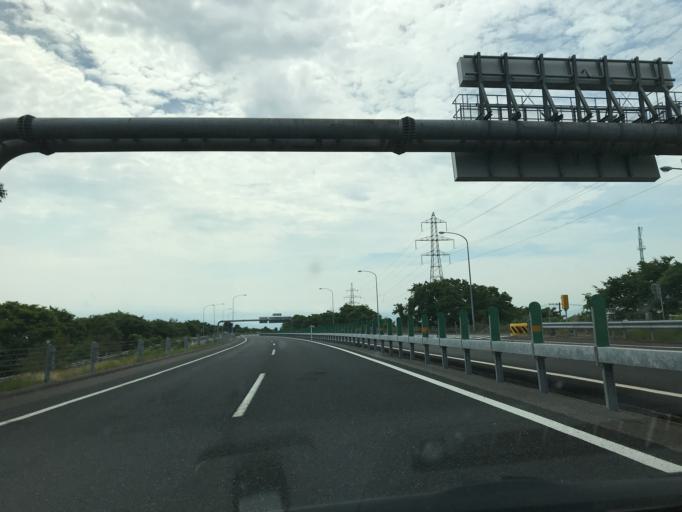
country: JP
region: Niigata
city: Niigata-shi
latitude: 37.8702
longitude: 139.0428
